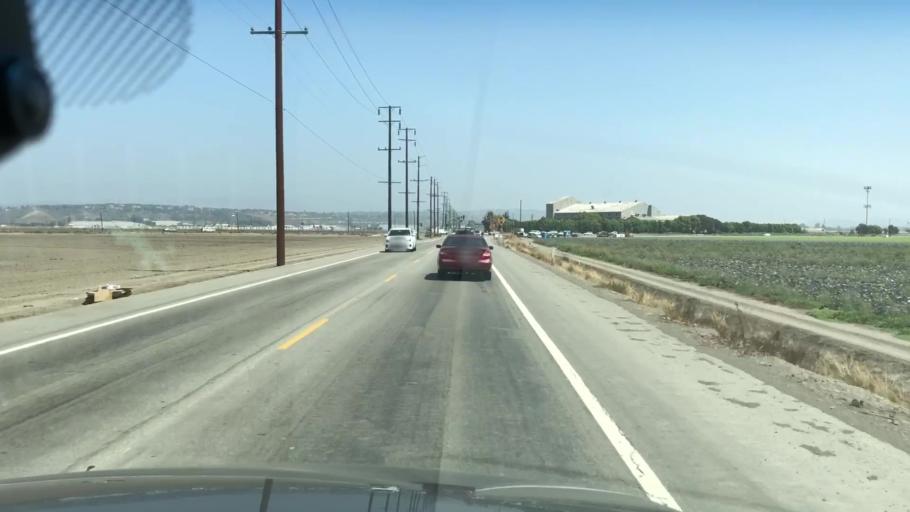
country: US
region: California
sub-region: Ventura County
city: Oxnard
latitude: 34.1942
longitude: -119.1067
